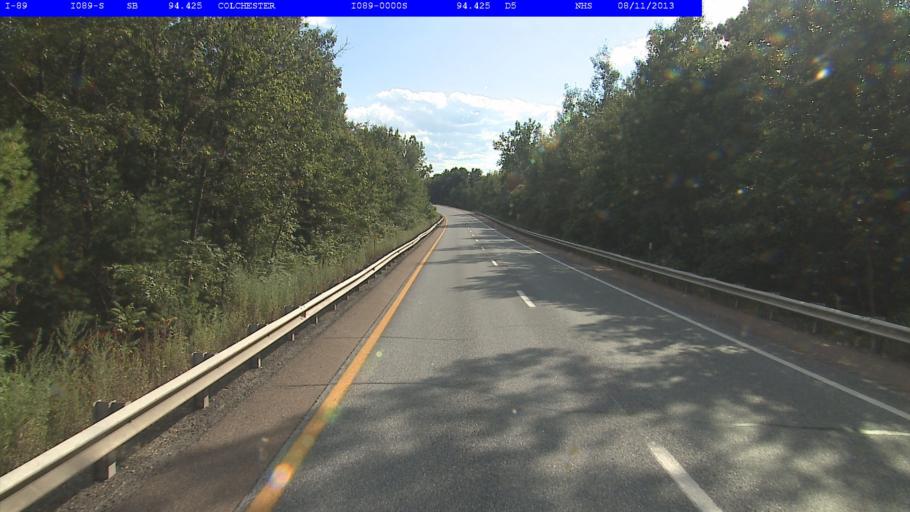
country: US
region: Vermont
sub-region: Chittenden County
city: Colchester
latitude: 44.5439
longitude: -73.1957
